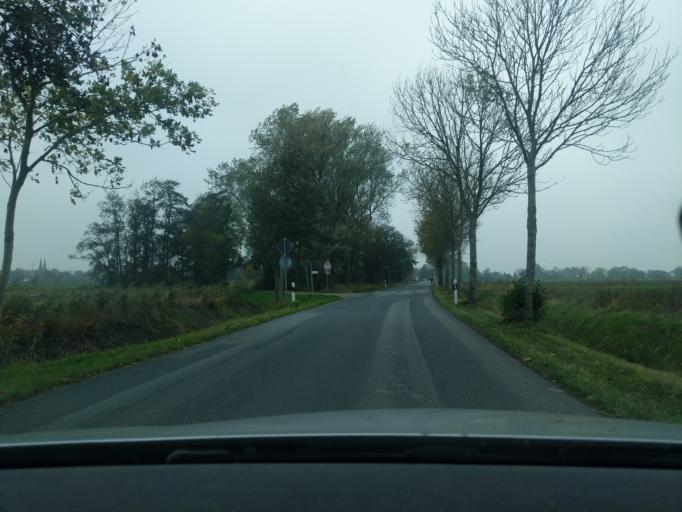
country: DE
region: Lower Saxony
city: Nordleda
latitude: 53.8272
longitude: 8.7863
